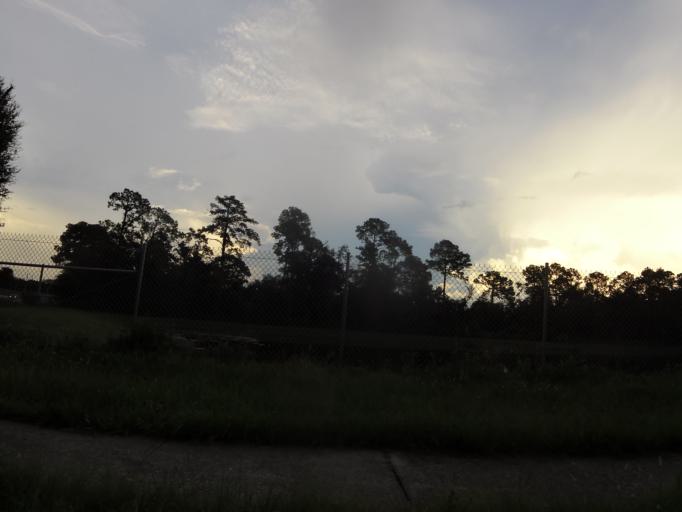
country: US
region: Florida
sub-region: Clay County
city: Bellair-Meadowbrook Terrace
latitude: 30.2696
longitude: -81.7722
